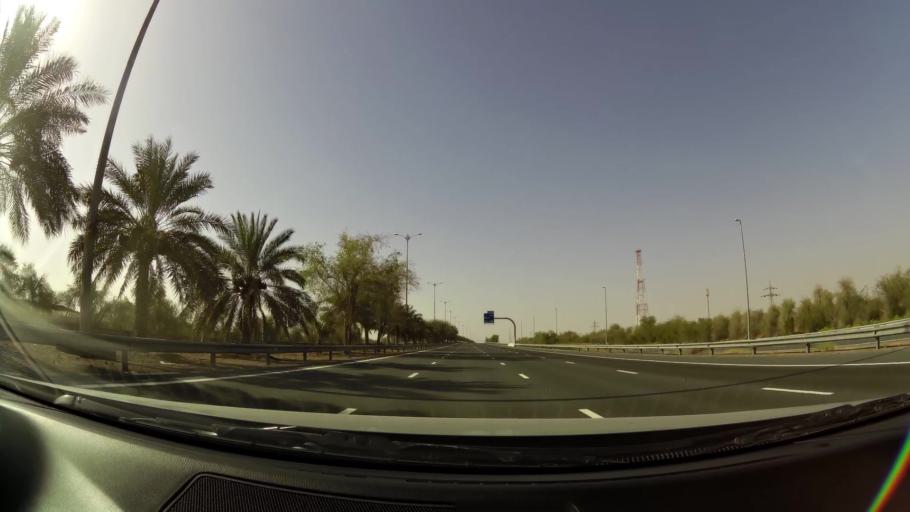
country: OM
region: Al Buraimi
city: Al Buraymi
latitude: 24.4186
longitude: 55.7915
